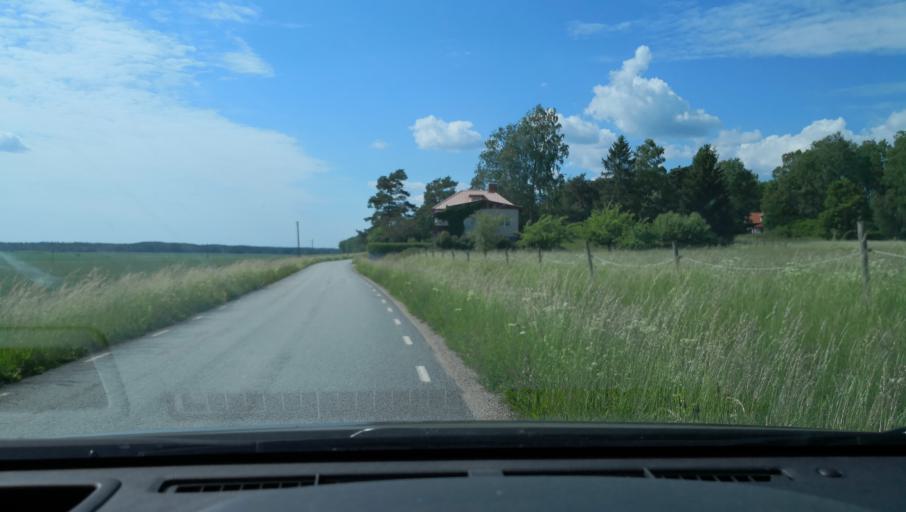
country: SE
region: Uppsala
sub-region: Enkopings Kommun
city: Orsundsbro
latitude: 59.8175
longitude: 17.3341
